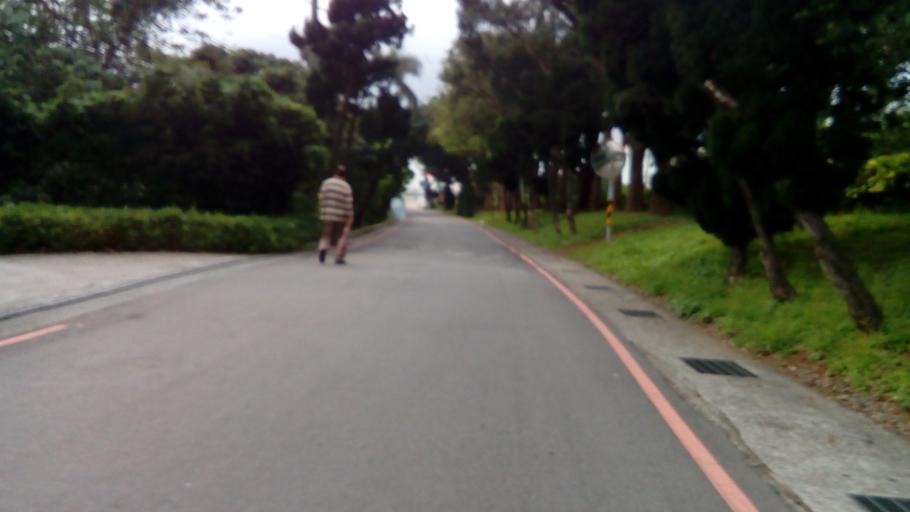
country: TW
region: Taipei
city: Taipei
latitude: 25.1776
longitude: 121.4287
